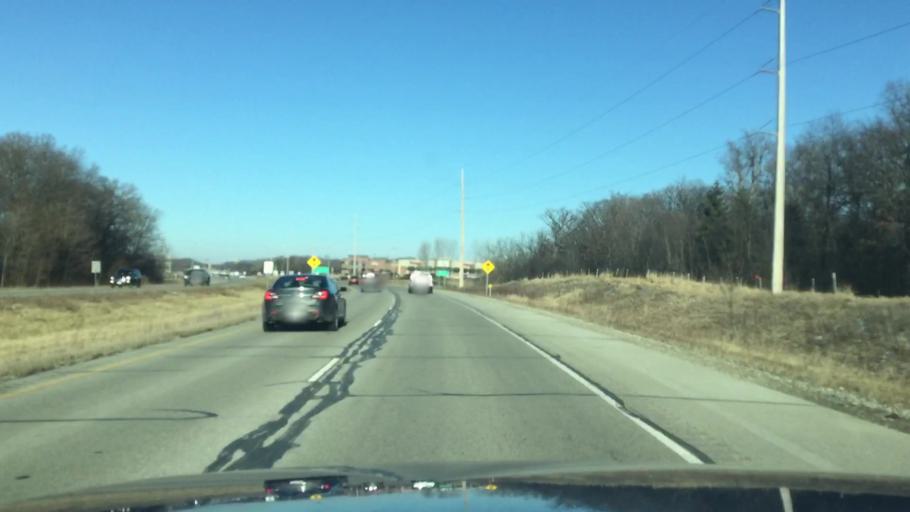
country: US
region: Wisconsin
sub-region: Racine County
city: Waterford
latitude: 42.7606
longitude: -88.2002
